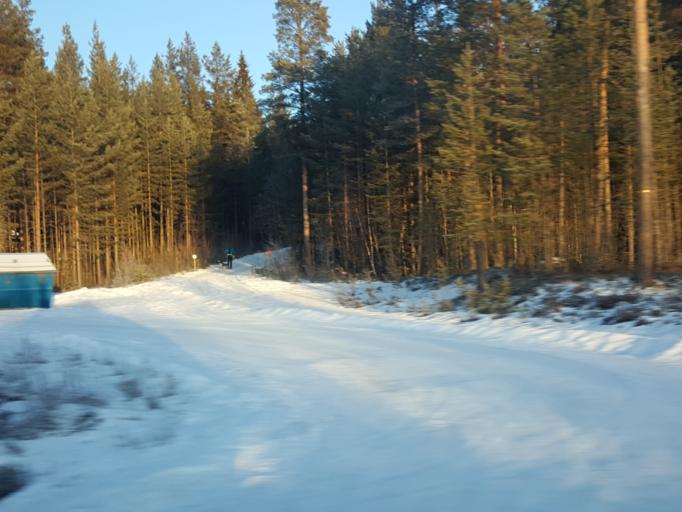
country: SE
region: Jaemtland
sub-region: Harjedalens Kommun
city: Sveg
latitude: 62.3882
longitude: 13.9496
